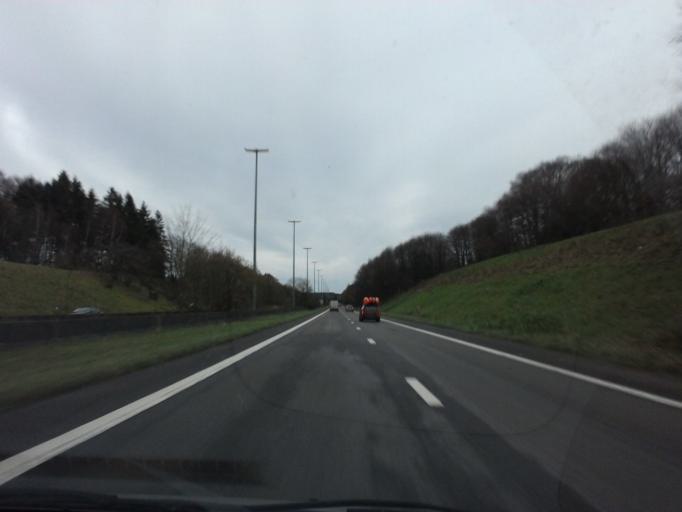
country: BE
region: Wallonia
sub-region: Province de Liege
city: Ferrieres
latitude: 50.3914
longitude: 5.6886
